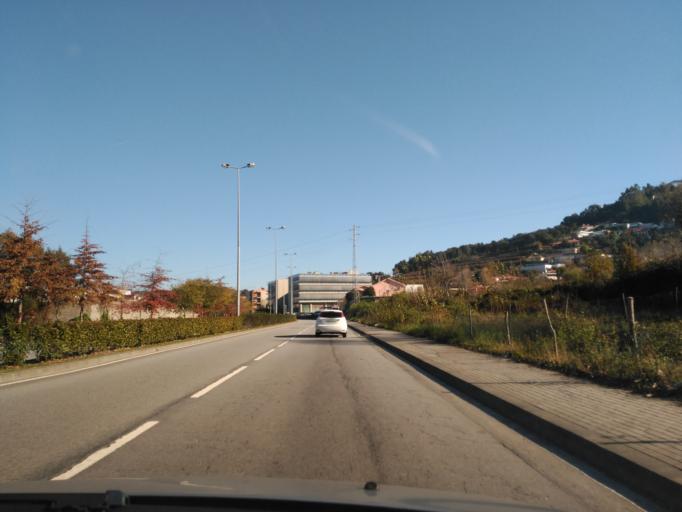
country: PT
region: Braga
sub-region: Braga
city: Adaufe
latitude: 41.5597
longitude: -8.3887
